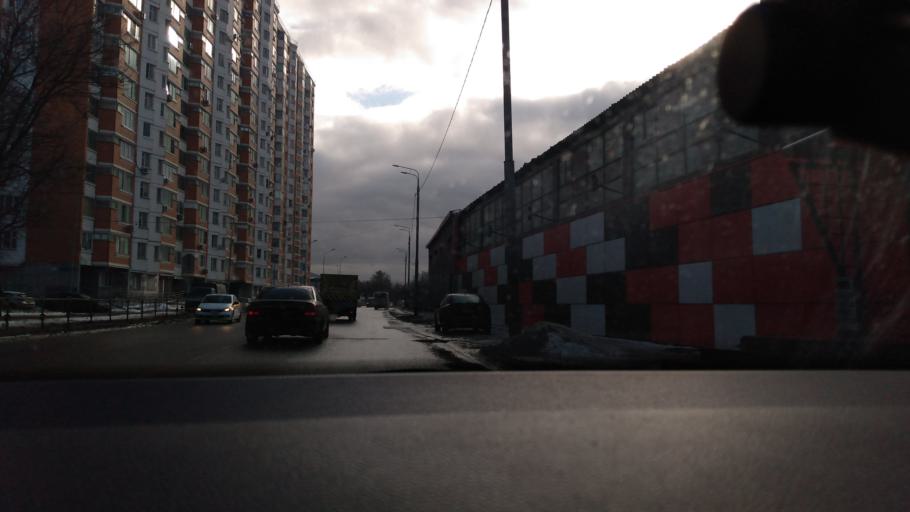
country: RU
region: Moskovskaya
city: Balashikha
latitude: 55.8180
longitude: 37.9529
